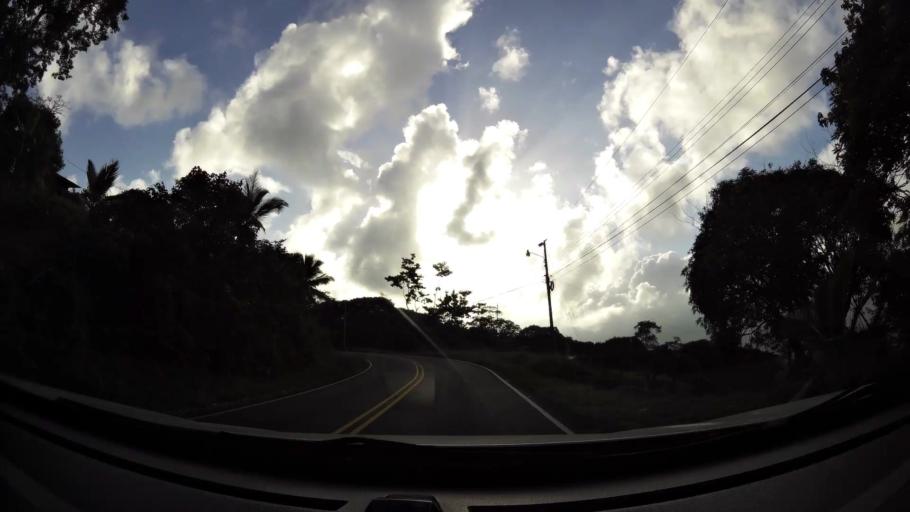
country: CR
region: Limon
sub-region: Canton de Siquirres
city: Siquirres
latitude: 10.0753
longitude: -83.5503
